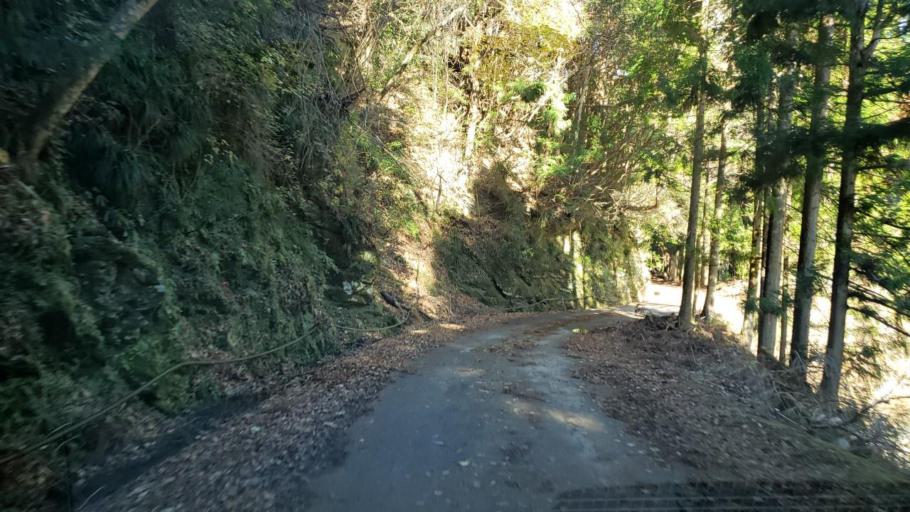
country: JP
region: Tokushima
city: Ikedacho
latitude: 33.9859
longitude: 133.9794
